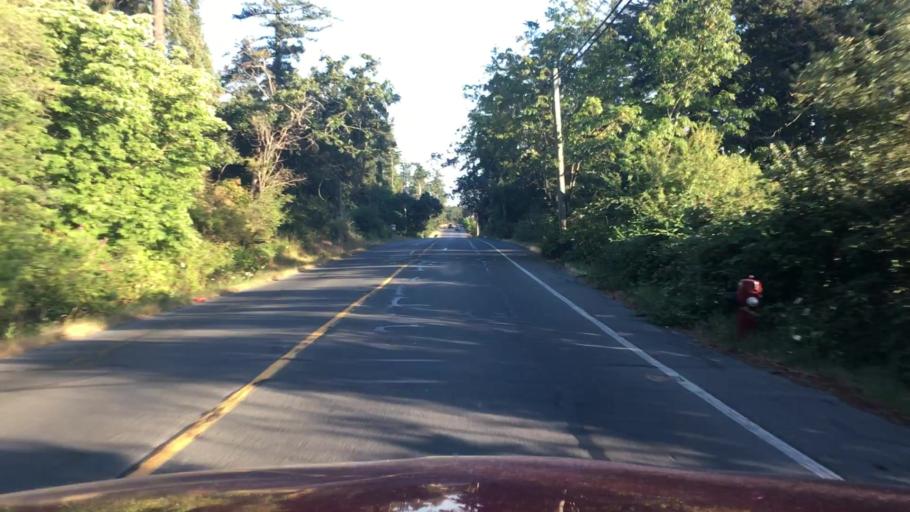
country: CA
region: British Columbia
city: Victoria
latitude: 48.4873
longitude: -123.3556
